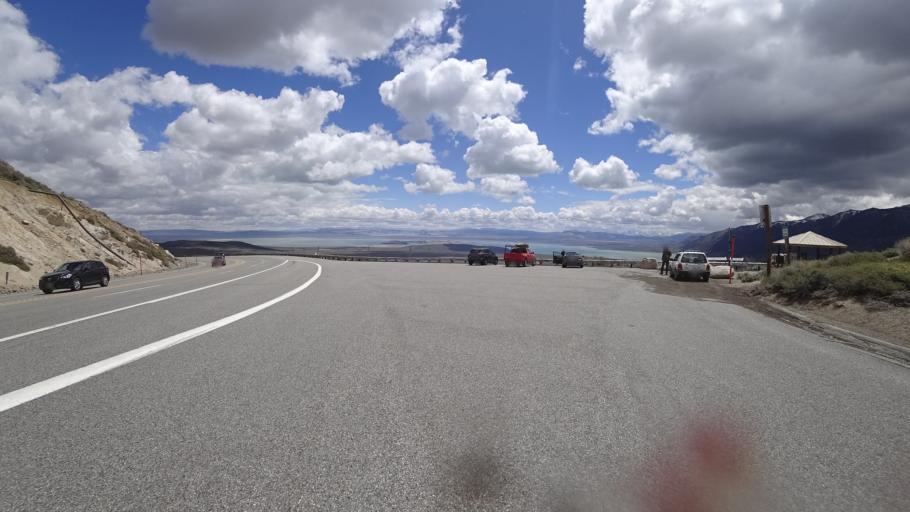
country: US
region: California
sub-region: Mono County
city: Bridgeport
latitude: 38.0743
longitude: -119.1771
